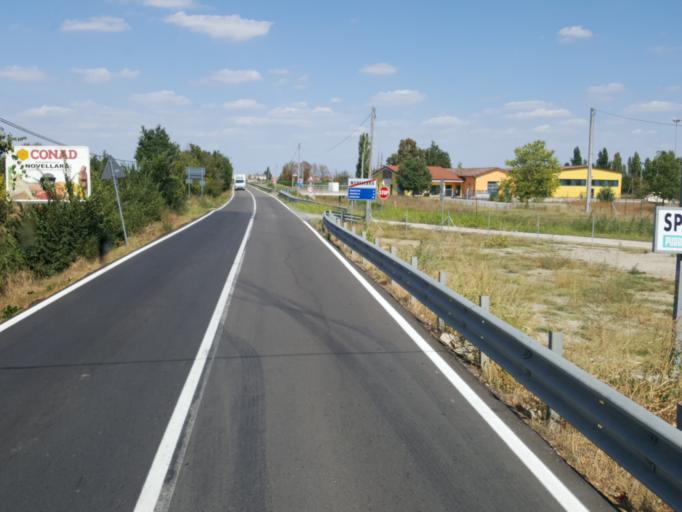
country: IT
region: Emilia-Romagna
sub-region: Provincia di Reggio Emilia
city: Novellara
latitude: 44.8581
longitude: 10.7440
